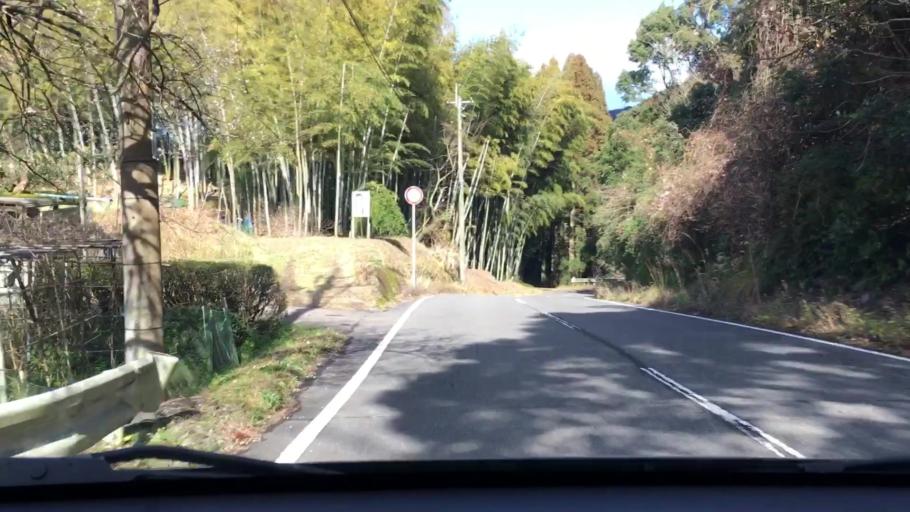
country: JP
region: Kagoshima
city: Ijuin
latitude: 31.7283
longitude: 130.4188
